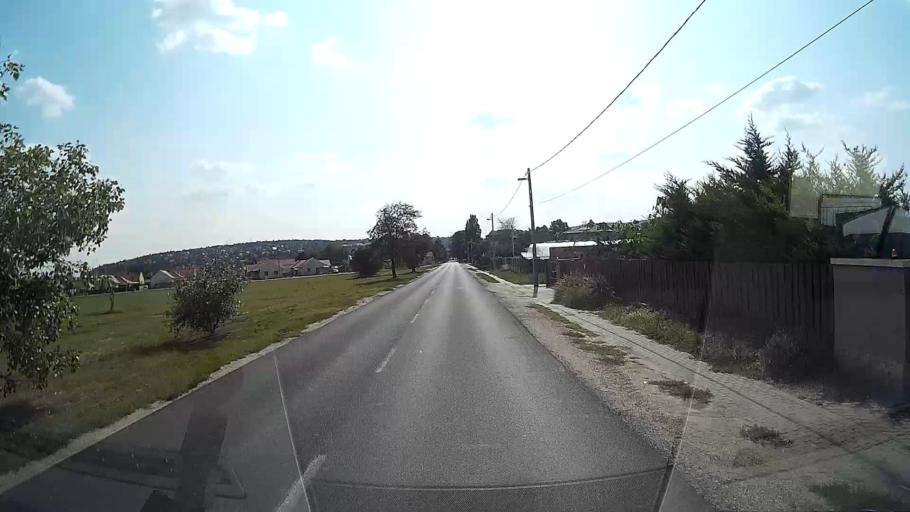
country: HU
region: Pest
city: Budakalasz
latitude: 47.6261
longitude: 19.0542
